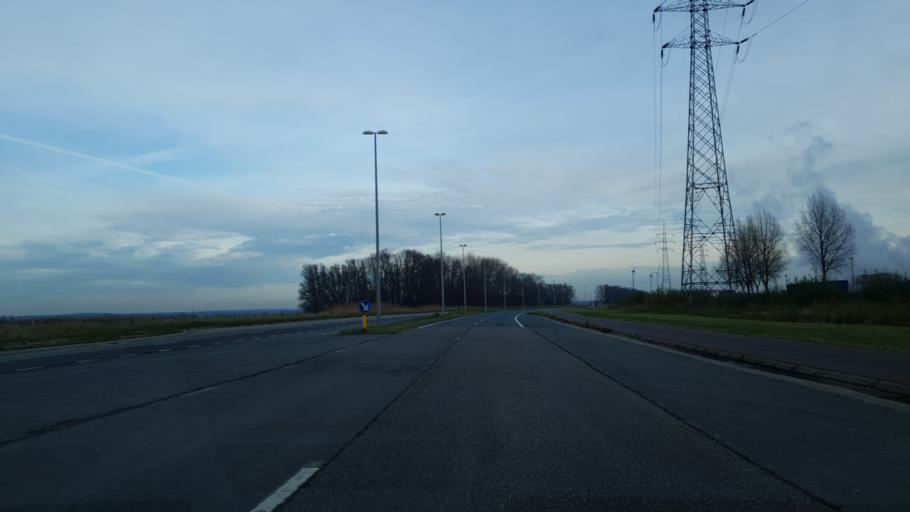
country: NL
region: North Brabant
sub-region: Gemeente Woensdrecht
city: Woensdrecht
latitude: 51.3747
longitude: 4.2602
